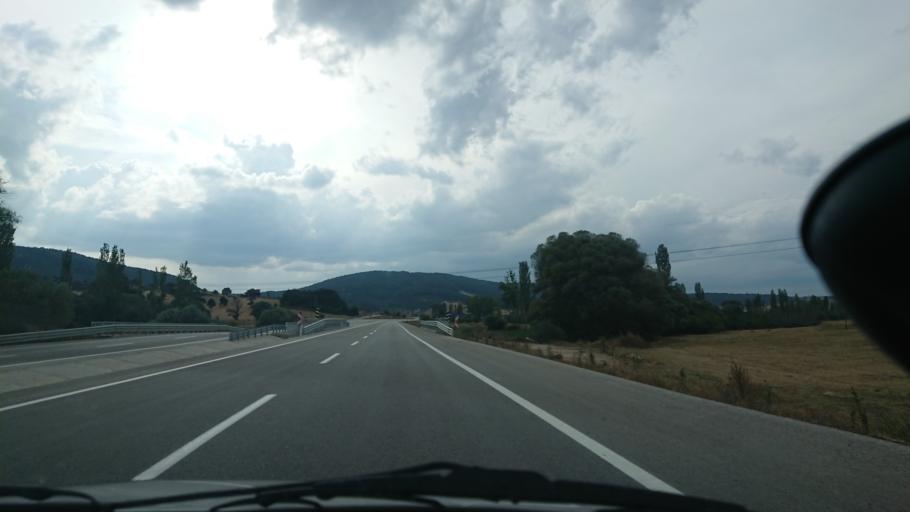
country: TR
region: Kuetahya
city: Cavdarhisar
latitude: 39.1053
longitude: 29.4958
